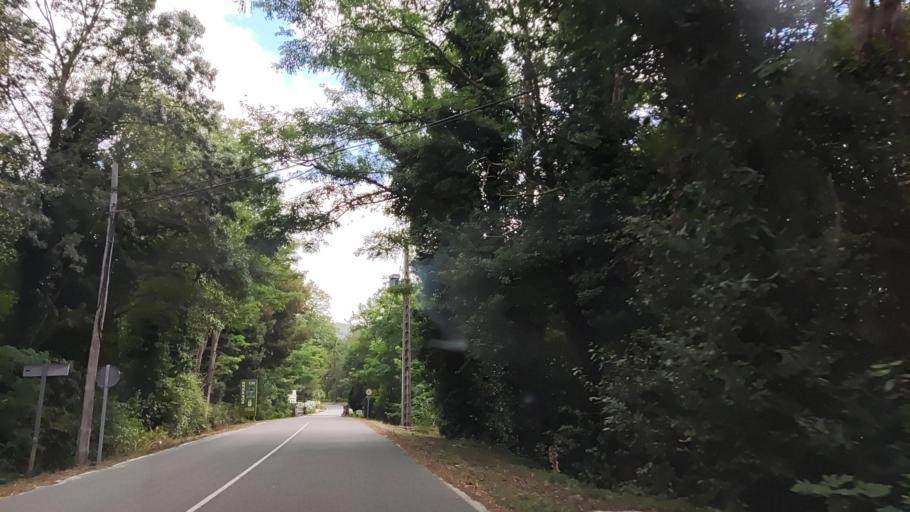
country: ES
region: Galicia
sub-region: Provincia da Coruna
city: Padron
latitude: 42.7818
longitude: -8.6655
